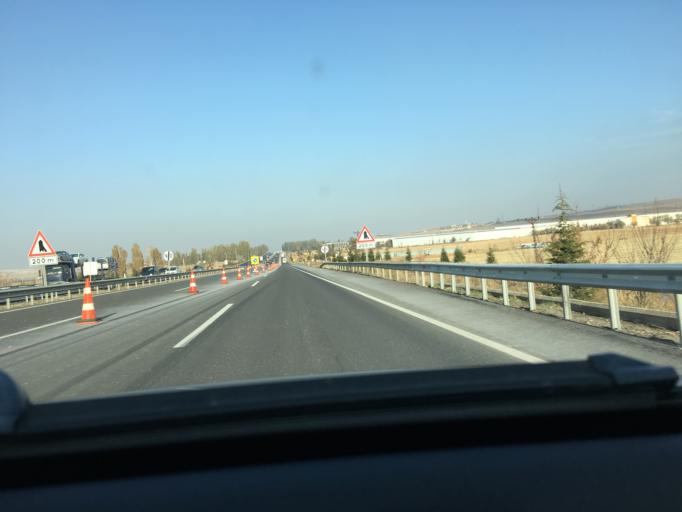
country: TR
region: Ankara
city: Temelli
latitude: 39.6827
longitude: 32.2427
